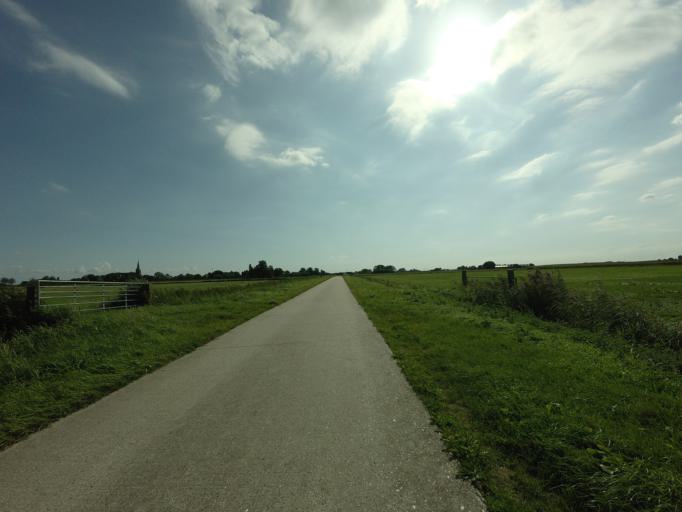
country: NL
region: Friesland
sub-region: Gemeente Littenseradiel
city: Makkum
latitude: 53.0811
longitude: 5.6317
